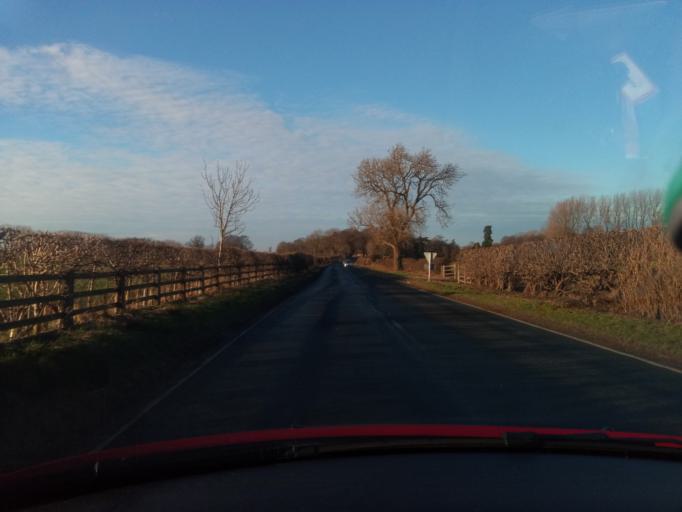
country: GB
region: England
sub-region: North Yorkshire
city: Thirsk
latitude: 54.2128
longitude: -1.4474
